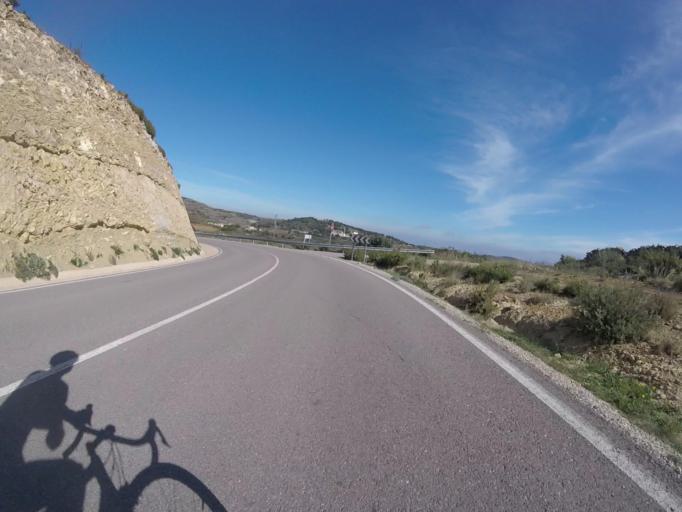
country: ES
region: Valencia
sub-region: Provincia de Castello
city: Sarratella
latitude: 40.3059
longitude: 0.0341
